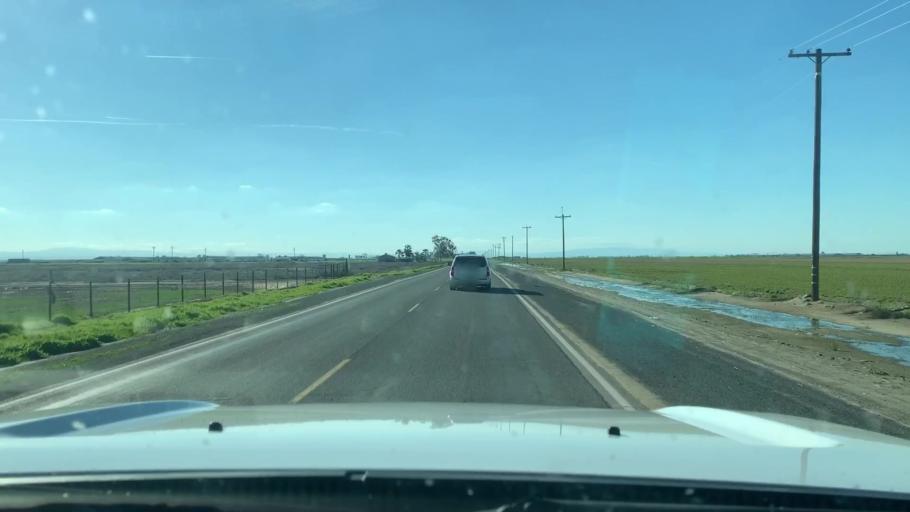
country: US
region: California
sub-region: Kings County
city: Home Garden
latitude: 36.2111
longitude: -119.6755
